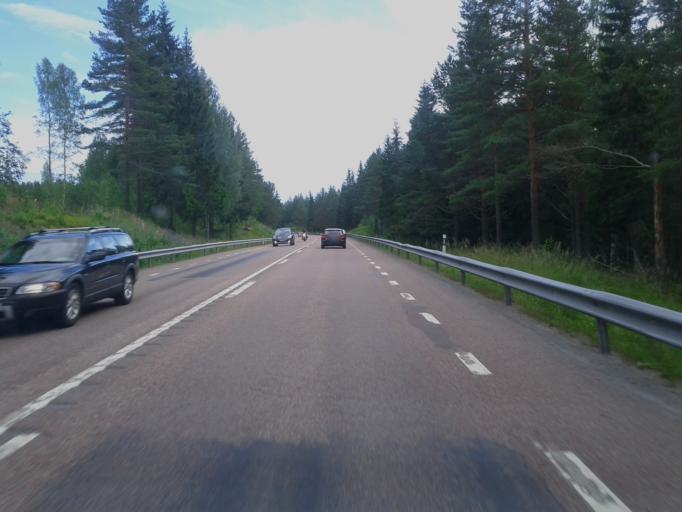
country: SE
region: Dalarna
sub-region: Faluns Kommun
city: Grycksbo
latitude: 60.7084
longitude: 15.4640
